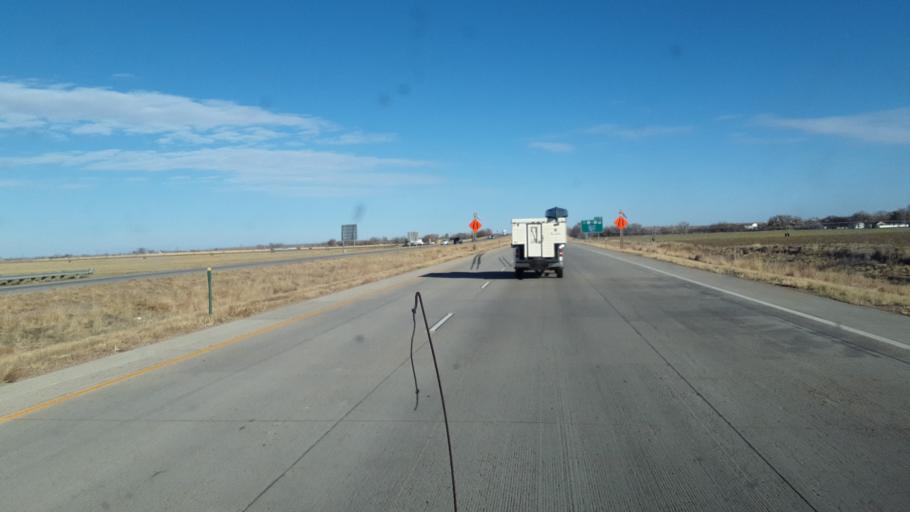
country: US
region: Colorado
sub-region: Morgan County
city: Brush
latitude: 40.2686
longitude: -103.6121
